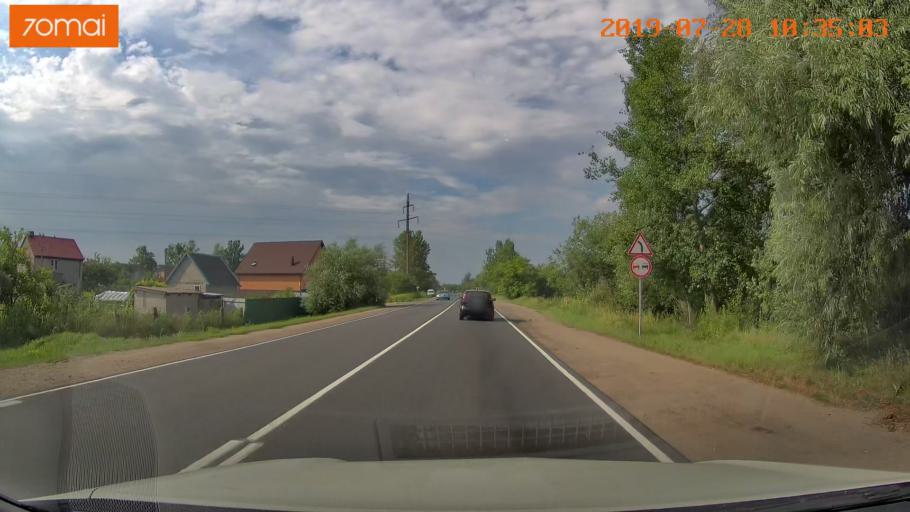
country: RU
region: Kaliningrad
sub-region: Gorod Kaliningrad
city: Kaliningrad
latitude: 54.7501
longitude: 20.4353
